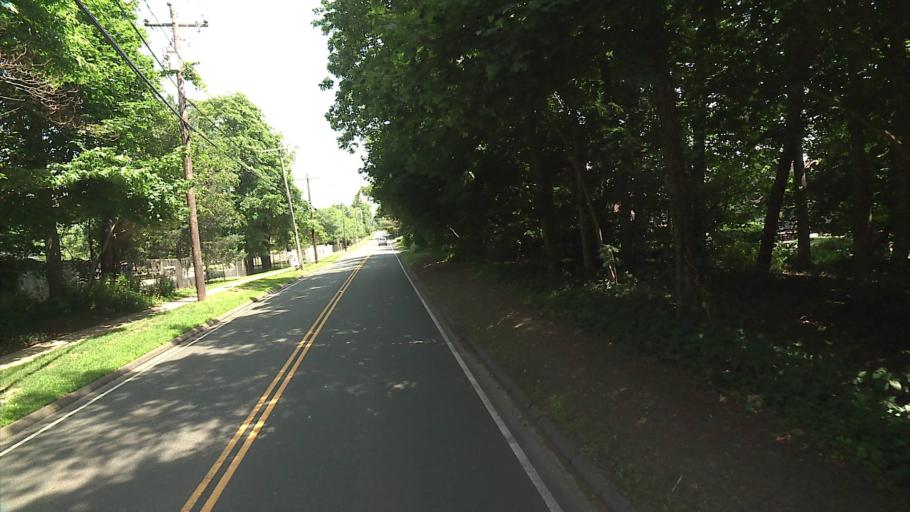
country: US
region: Connecticut
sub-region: New Haven County
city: Branford
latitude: 41.2972
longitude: -72.8202
